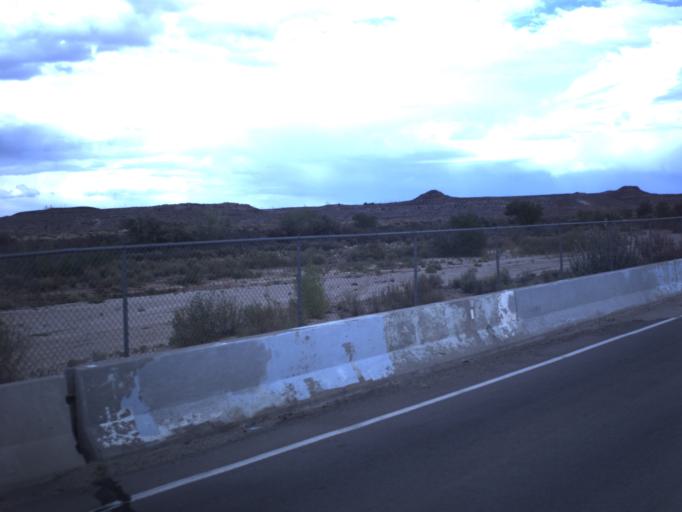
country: US
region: Utah
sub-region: San Juan County
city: Blanding
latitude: 37.2722
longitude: -109.3285
